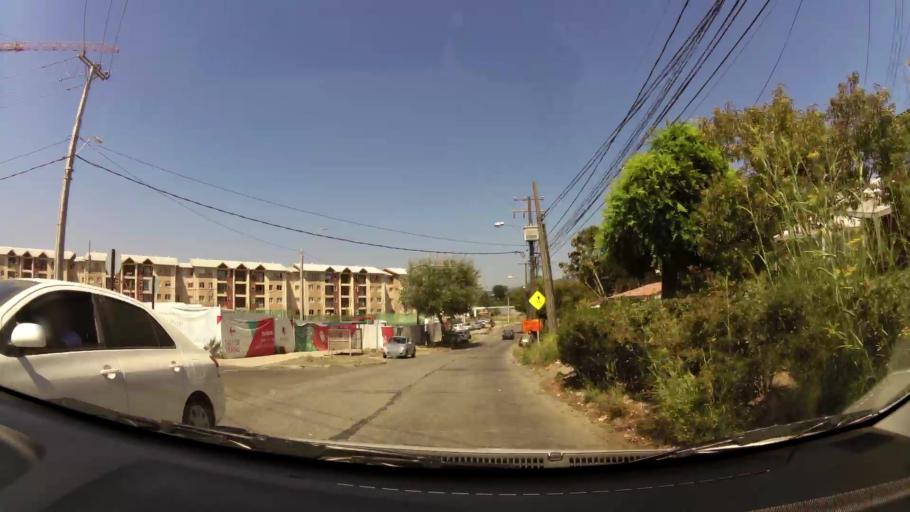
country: CL
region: Biobio
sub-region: Provincia de Concepcion
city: Concepcion
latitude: -36.8076
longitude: -73.0603
